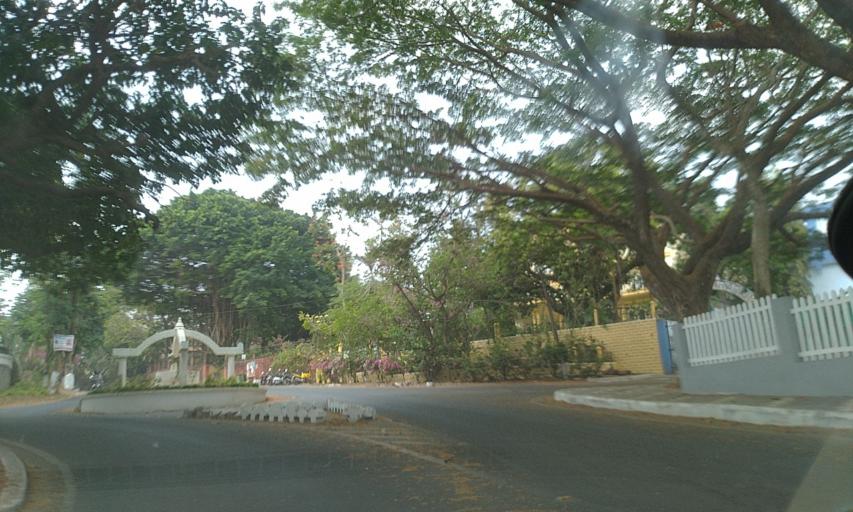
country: IN
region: Goa
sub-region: North Goa
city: Panaji
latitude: 15.4931
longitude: 73.8243
